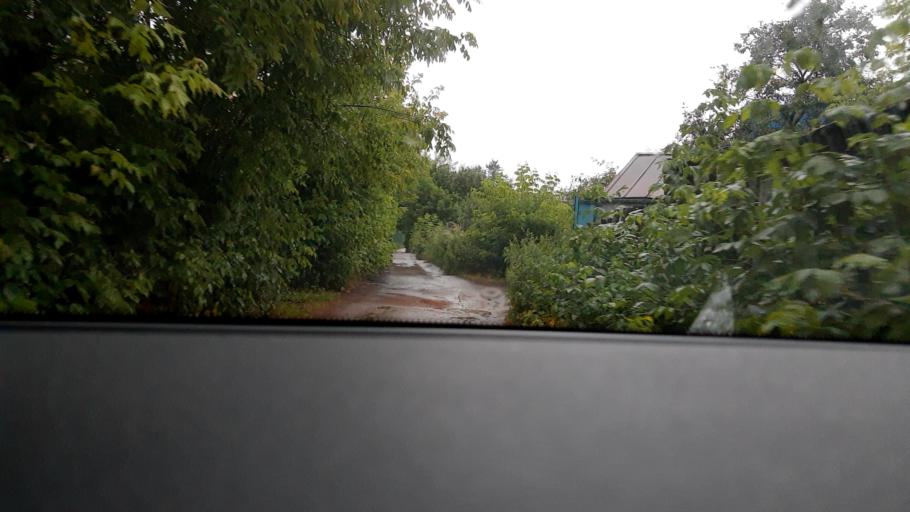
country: RU
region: Nizjnij Novgorod
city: Gorbatovka
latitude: 56.2603
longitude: 43.8271
